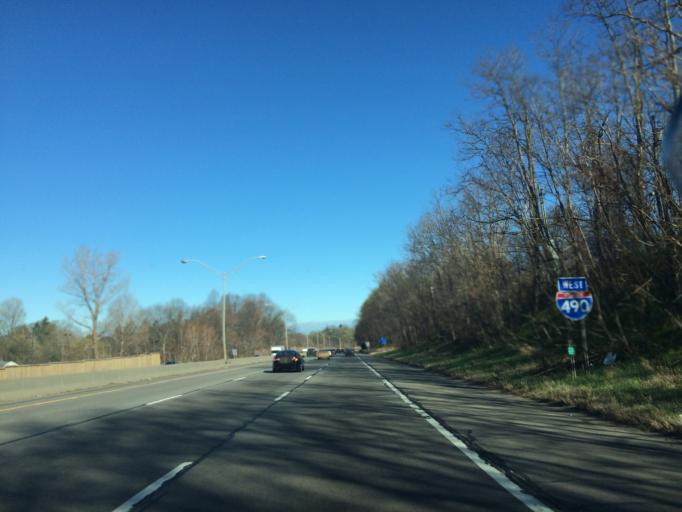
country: US
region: New York
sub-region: Monroe County
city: Pittsford
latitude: 43.1211
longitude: -77.5185
